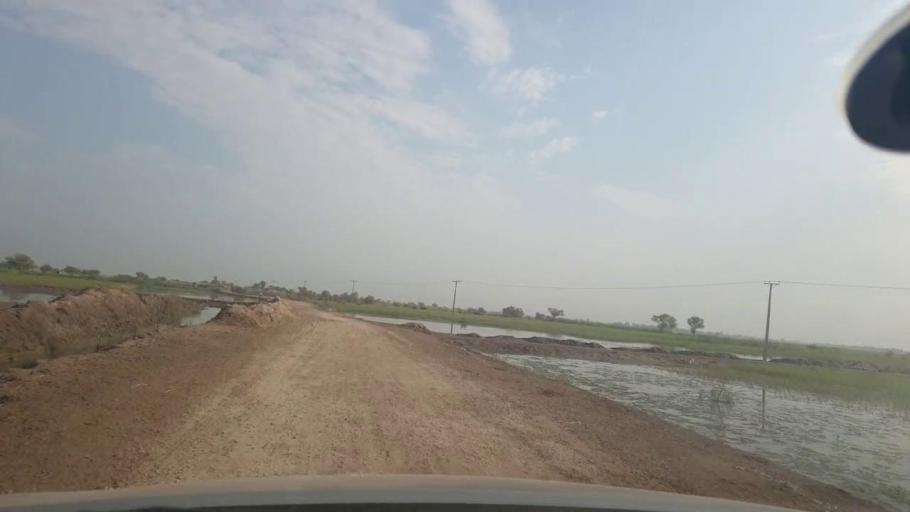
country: PK
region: Balochistan
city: Mehrabpur
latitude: 28.0682
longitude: 68.2106
